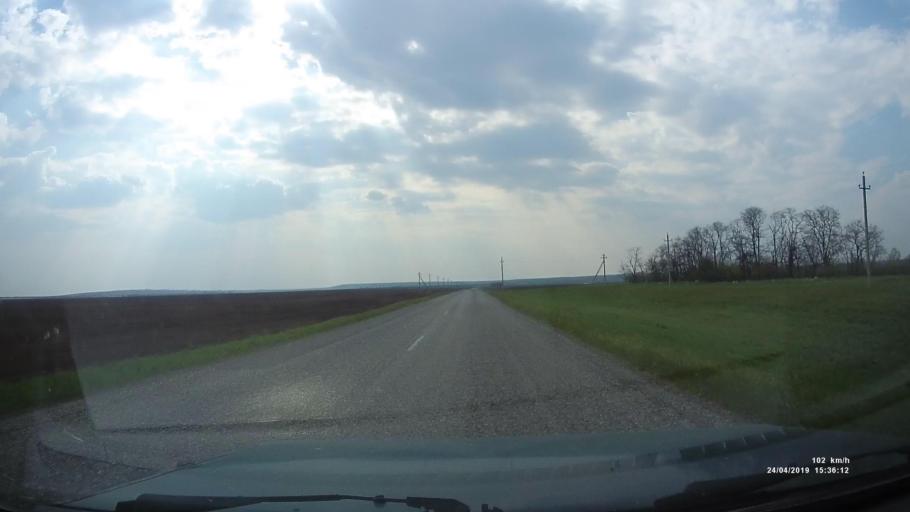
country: RU
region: Kalmykiya
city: Yashalta
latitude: 46.5992
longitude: 42.8769
